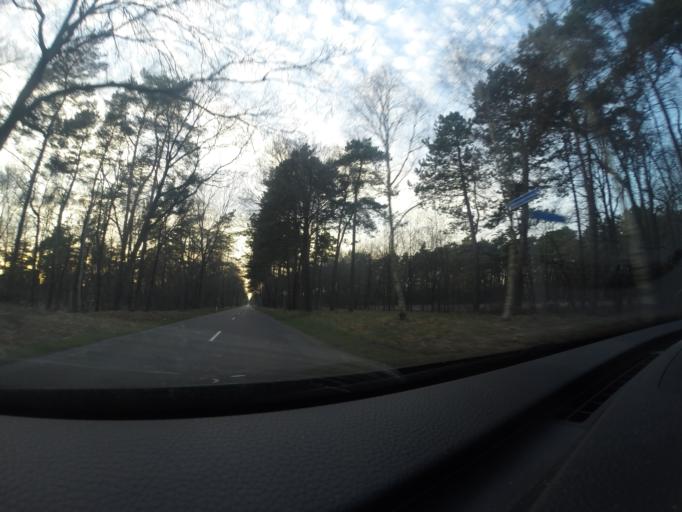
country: NL
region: Overijssel
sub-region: Gemeente Haaksbergen
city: Haaksbergen
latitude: 52.1510
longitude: 6.7810
